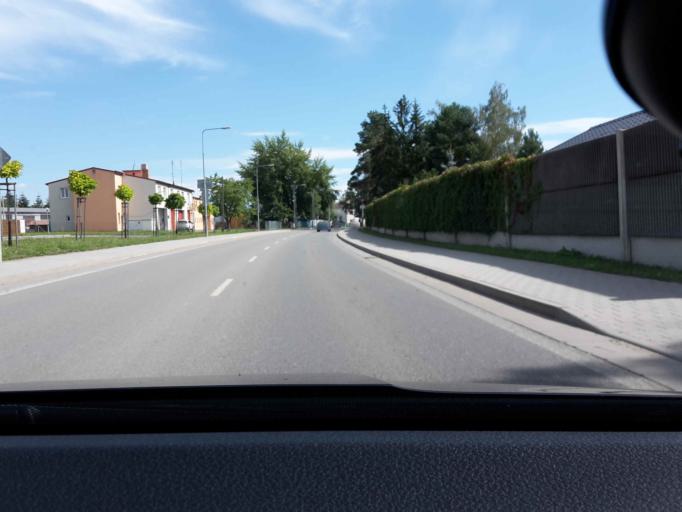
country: CZ
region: Jihocesky
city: Sobeslav
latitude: 49.2630
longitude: 14.7210
